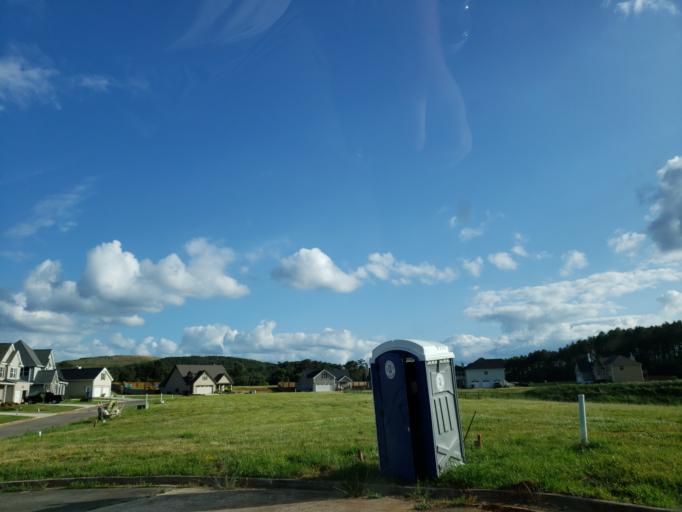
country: US
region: Georgia
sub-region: Bartow County
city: Adairsville
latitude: 34.3901
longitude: -84.8955
